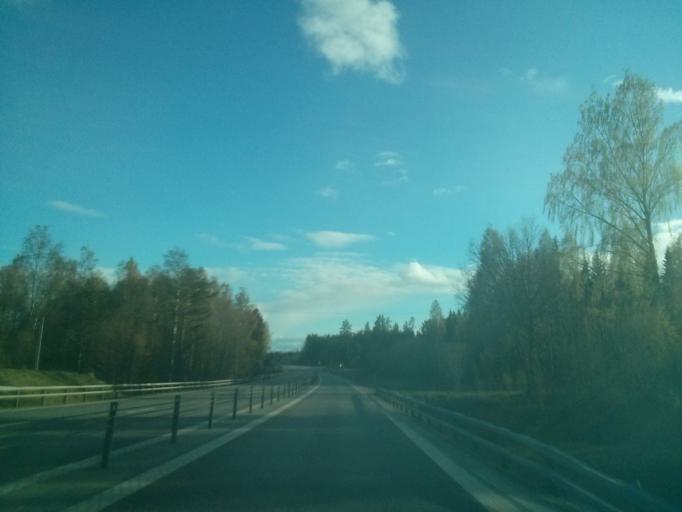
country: SE
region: Vaesternorrland
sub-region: Sundsvalls Kommun
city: Njurundabommen
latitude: 62.1570
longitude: 17.3514
